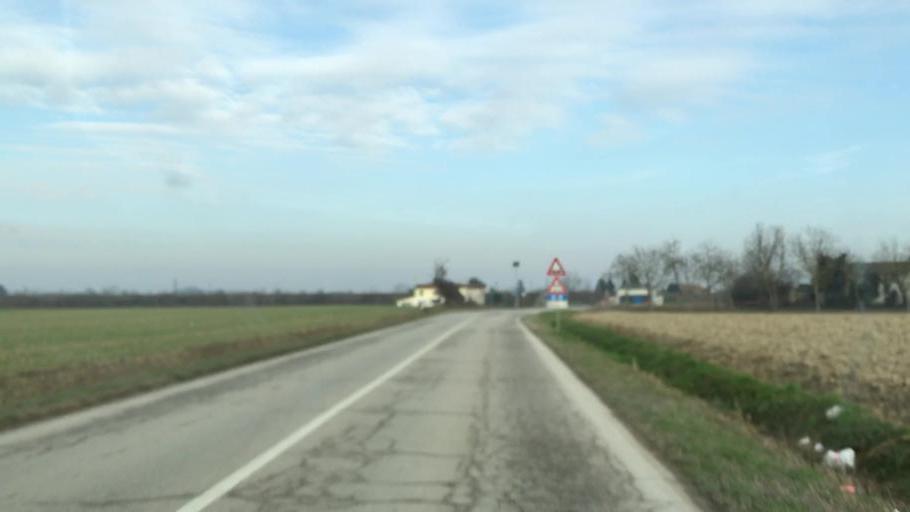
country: IT
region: Veneto
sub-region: Provincia di Rovigo
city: Fratta Polesine
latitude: 45.0351
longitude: 11.6509
